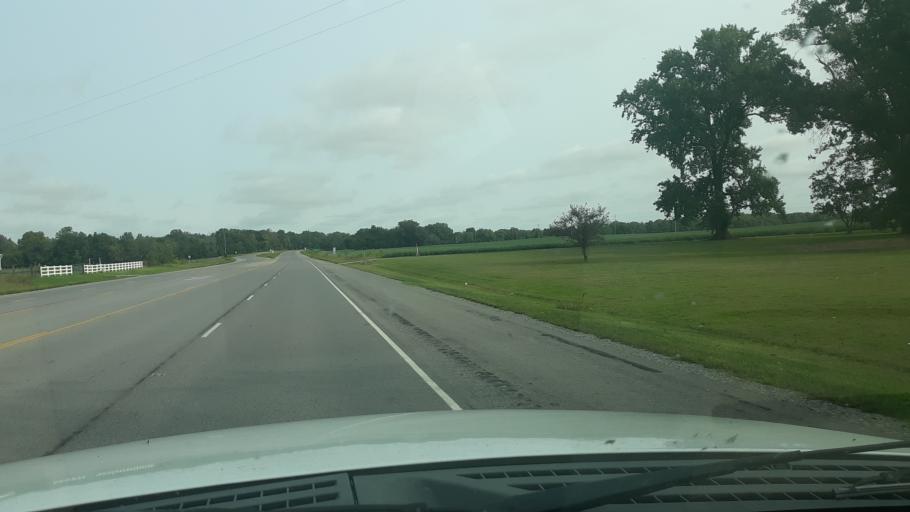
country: US
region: Illinois
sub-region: Saline County
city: Eldorado
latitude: 37.8151
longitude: -88.4268
